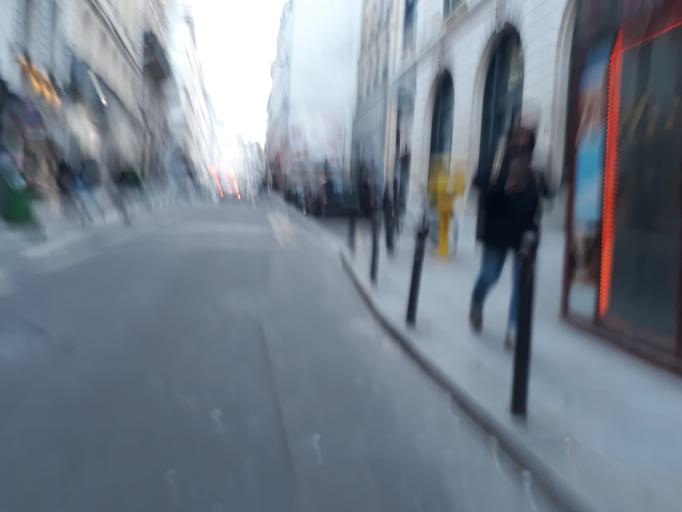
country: FR
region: Ile-de-France
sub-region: Paris
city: Paris
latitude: 48.8699
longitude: 2.3478
